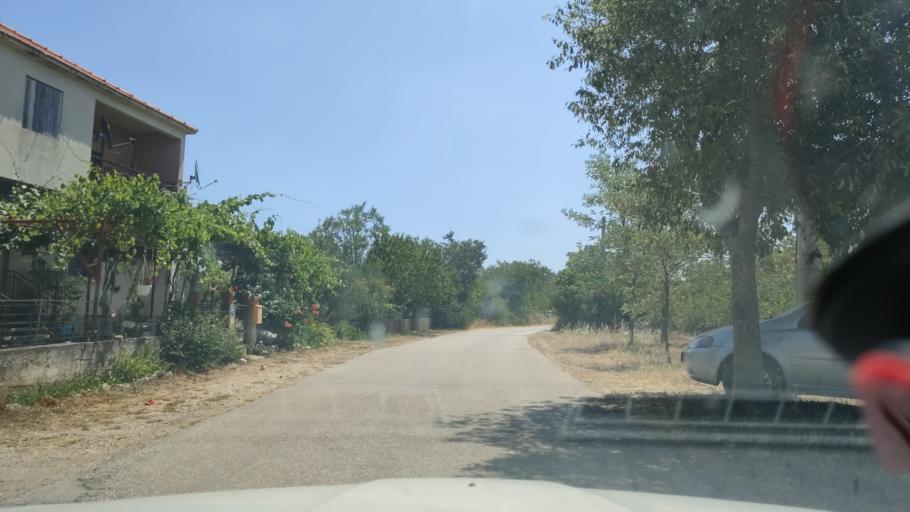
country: HR
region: Sibensko-Kniniska
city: Kistanje
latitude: 43.9579
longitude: 15.8763
